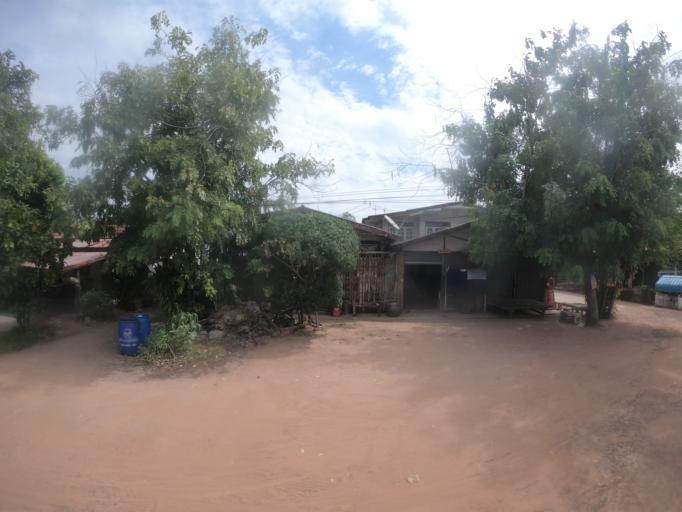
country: TH
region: Maha Sarakham
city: Chiang Yuen
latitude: 16.3675
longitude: 103.1060
